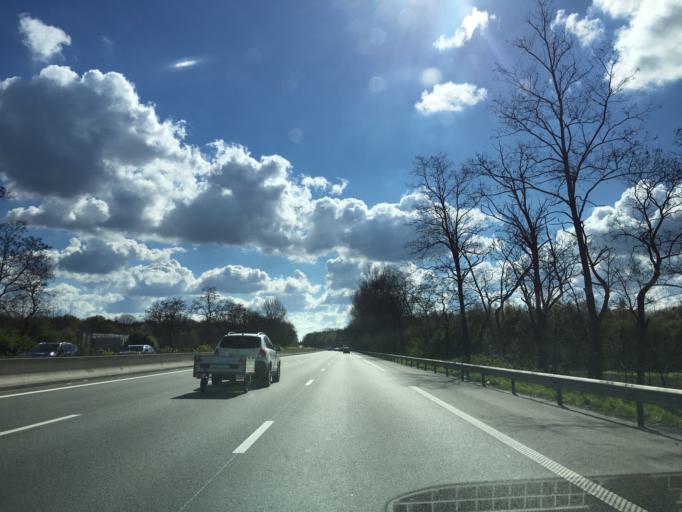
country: FR
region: Nord-Pas-de-Calais
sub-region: Departement du Nord
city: Camphin-en-Carembault
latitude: 50.4934
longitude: 2.9954
